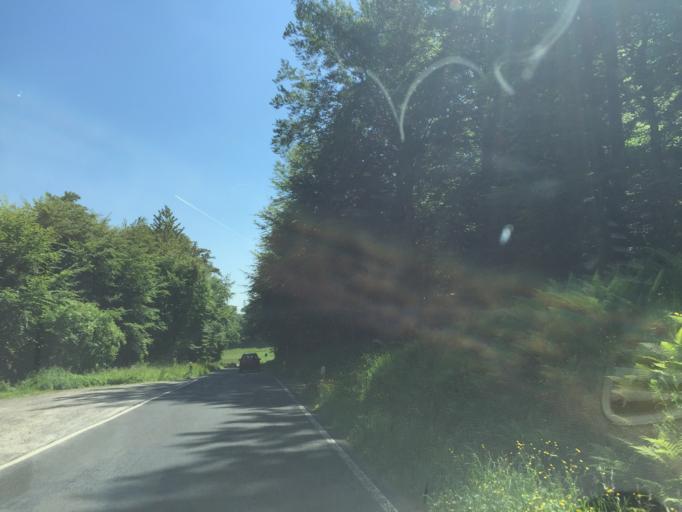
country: DE
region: Bavaria
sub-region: Regierungsbezirk Unterfranken
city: Miltenberg
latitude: 49.6570
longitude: 9.2700
